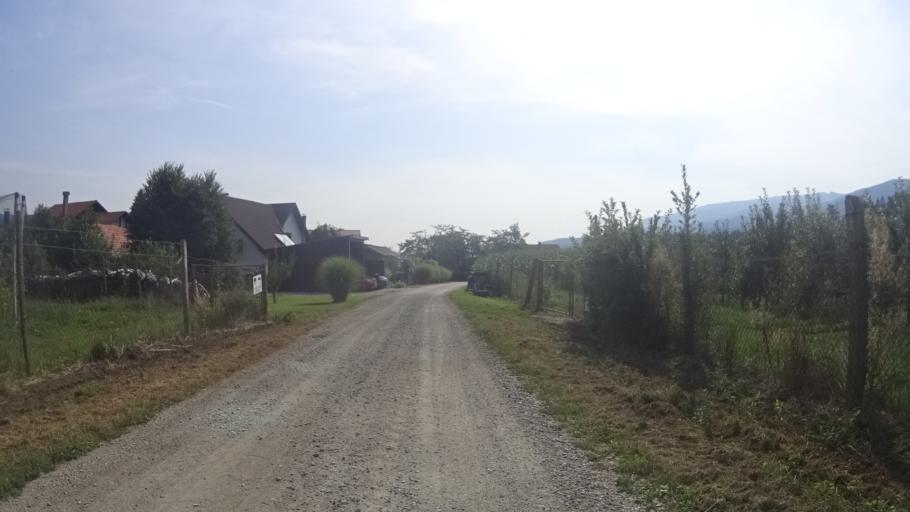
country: SI
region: Selnica ob Dravi
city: Selnica ob Dravi
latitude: 46.5443
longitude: 15.4816
